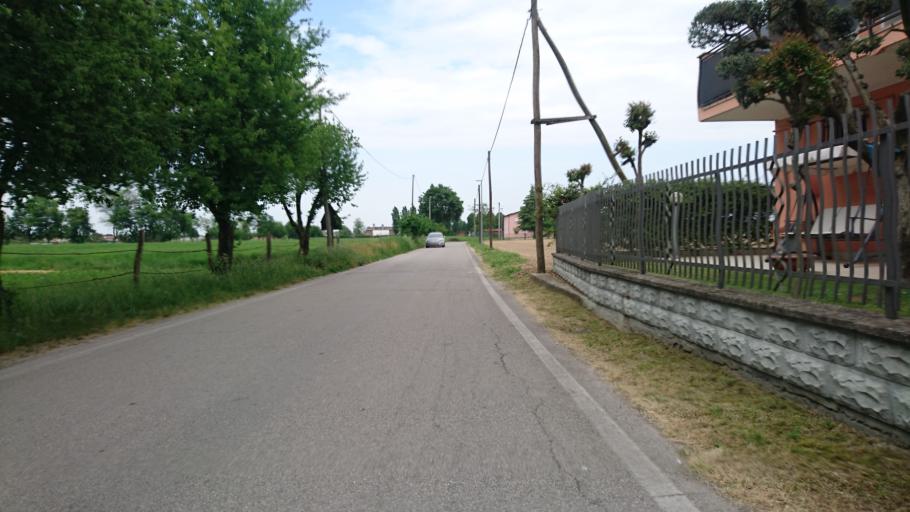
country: IT
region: Veneto
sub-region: Provincia di Padova
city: Montegrotto Terme
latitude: 45.3303
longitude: 11.8012
